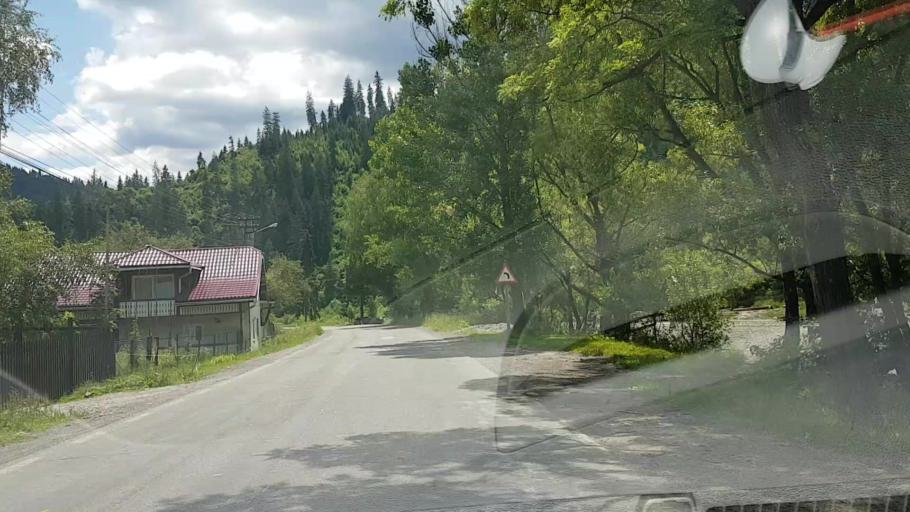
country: RO
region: Suceava
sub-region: Comuna Brosteni
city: Brosteni
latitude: 47.2409
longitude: 25.6910
